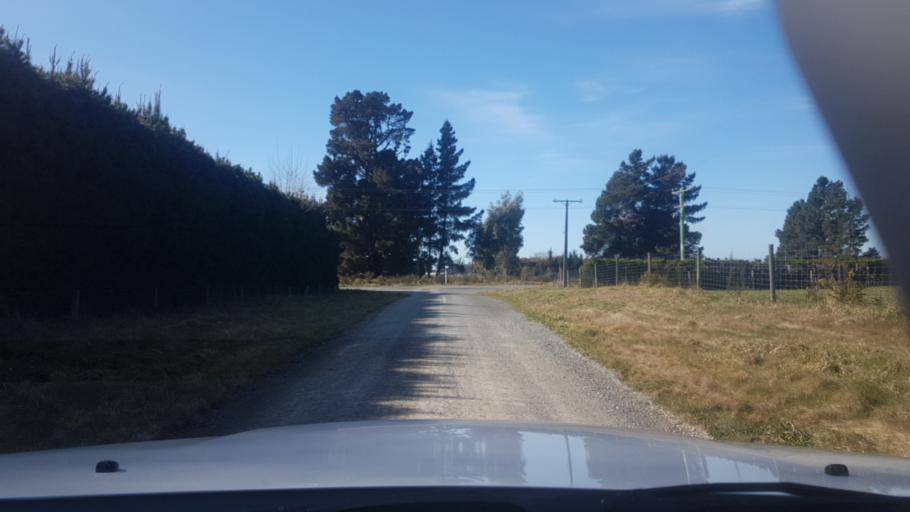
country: NZ
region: Canterbury
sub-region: Timaru District
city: Pleasant Point
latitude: -44.1472
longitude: 171.2902
